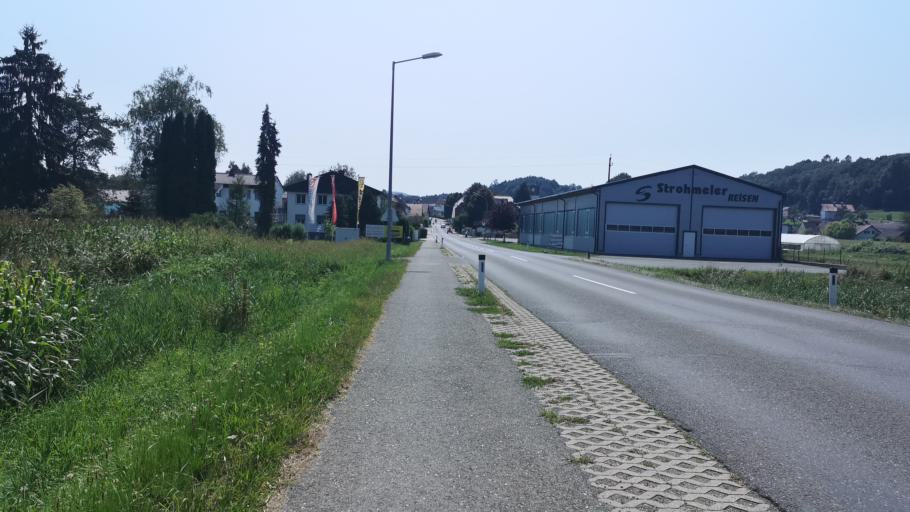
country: AT
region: Styria
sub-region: Politischer Bezirk Deutschlandsberg
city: Wettmannstatten
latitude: 46.8338
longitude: 15.3828
